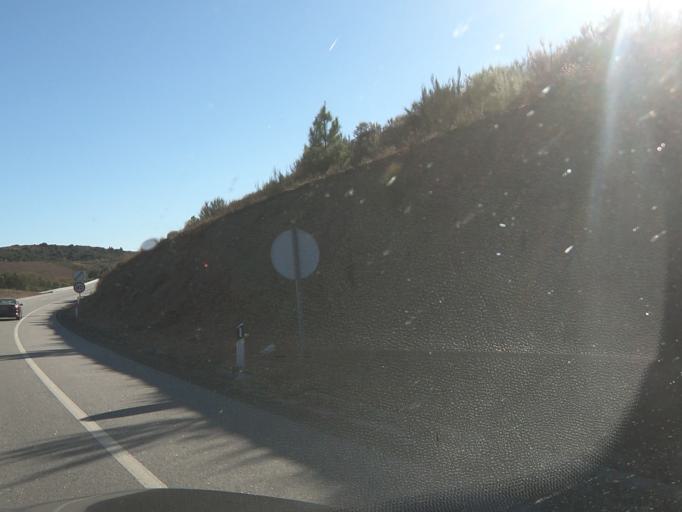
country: PT
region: Braganca
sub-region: Mirandela
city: Mirandela
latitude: 41.5138
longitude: -7.2272
